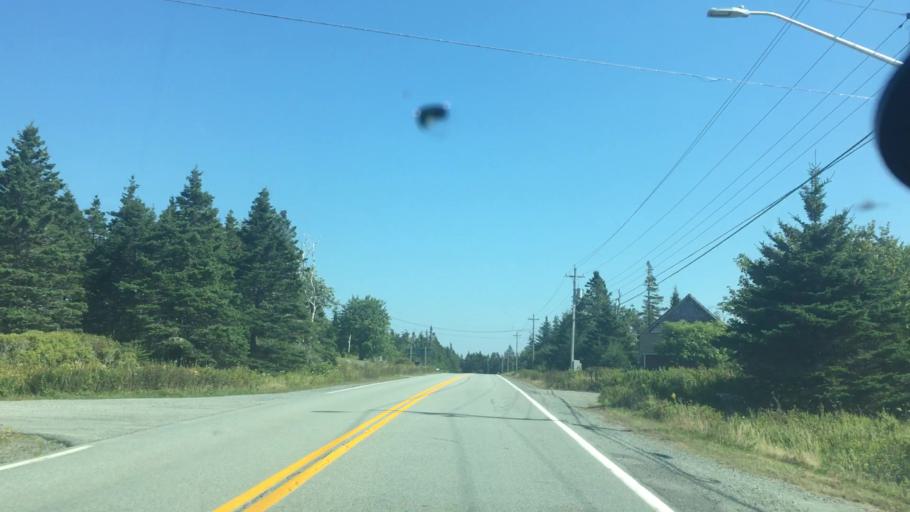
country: CA
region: Nova Scotia
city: New Glasgow
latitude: 44.9213
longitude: -62.3029
